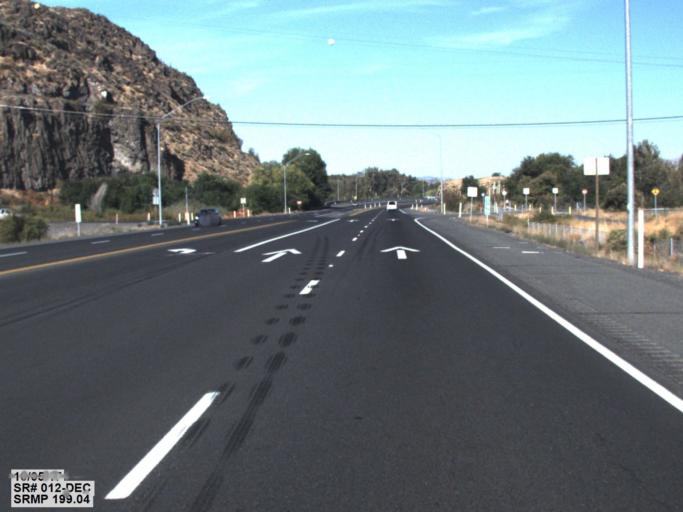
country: US
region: Washington
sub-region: Yakima County
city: Gleed
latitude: 46.6289
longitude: -120.5802
